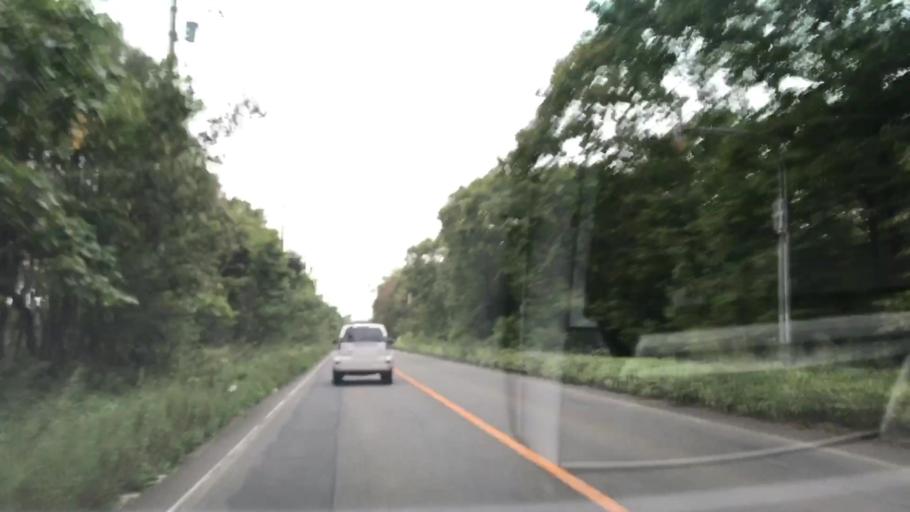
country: JP
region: Hokkaido
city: Tomakomai
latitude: 42.7051
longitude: 141.6659
